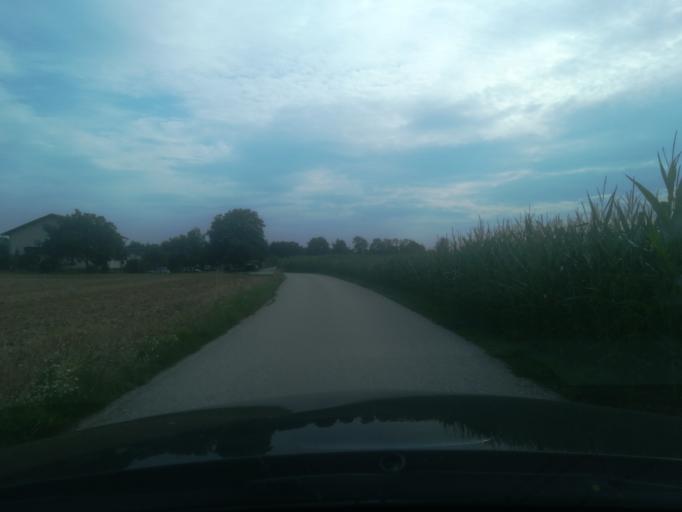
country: AT
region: Upper Austria
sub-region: Wels-Land
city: Marchtrenk
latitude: 48.1841
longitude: 14.1317
